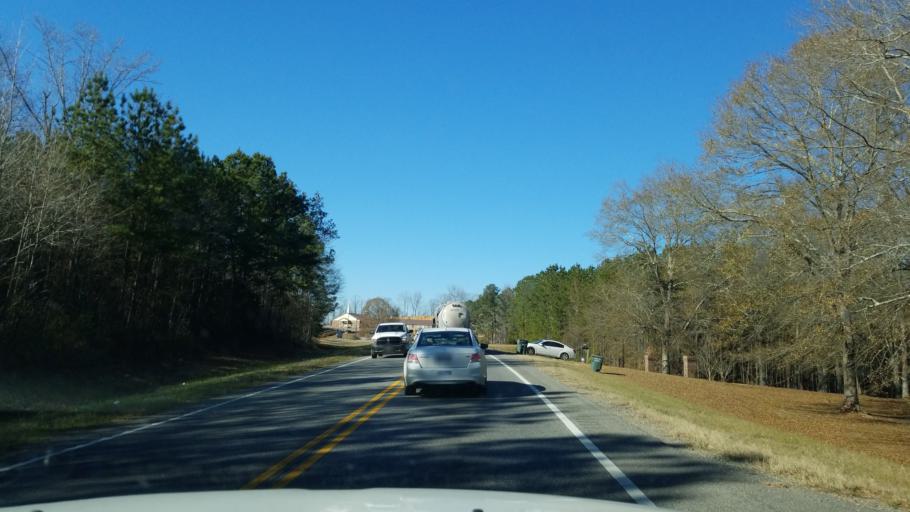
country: US
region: Alabama
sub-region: Pickens County
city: Gordo
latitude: 33.3305
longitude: -87.9132
